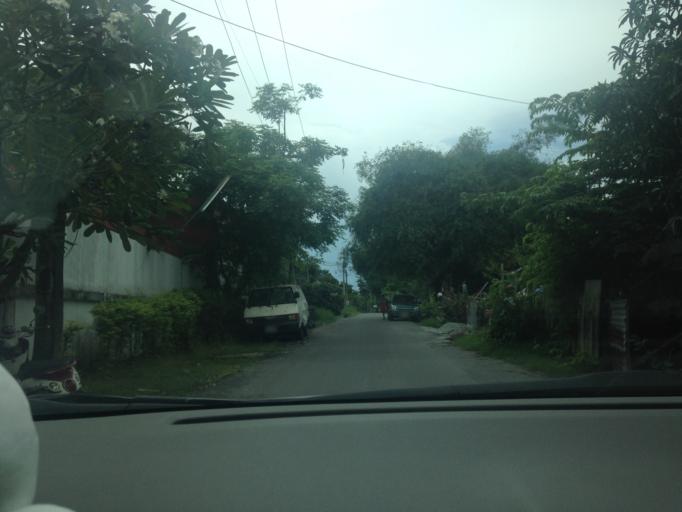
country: TH
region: Chon Buri
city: Chon Buri
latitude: 13.3277
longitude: 100.9269
